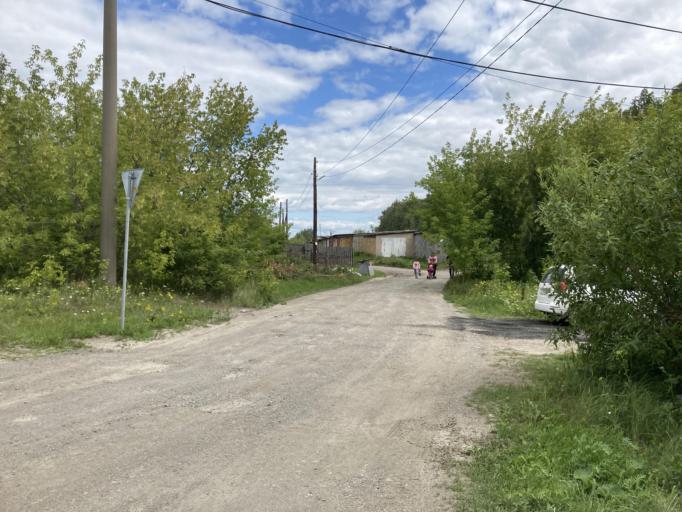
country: RU
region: Sverdlovsk
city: Bogdanovich
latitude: 56.7792
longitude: 62.0628
